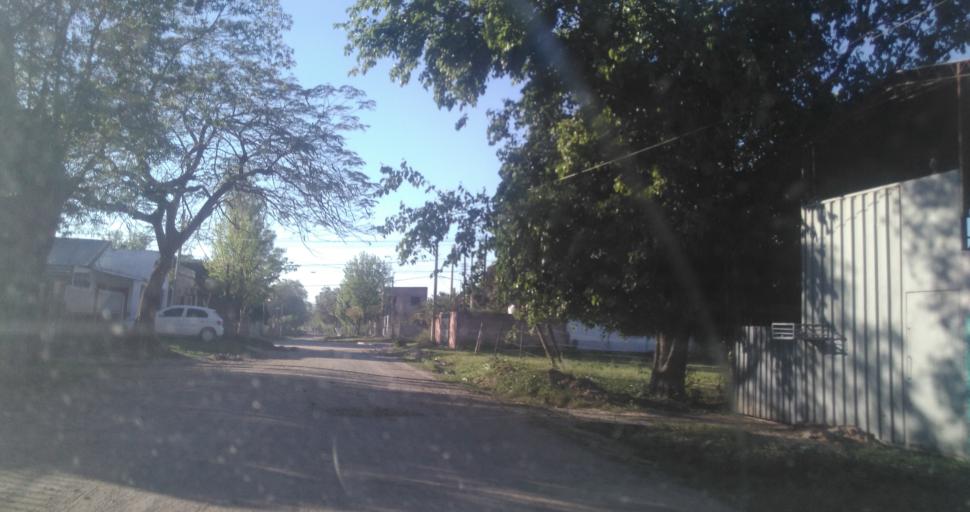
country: AR
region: Chaco
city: Fontana
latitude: -27.4245
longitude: -59.0227
